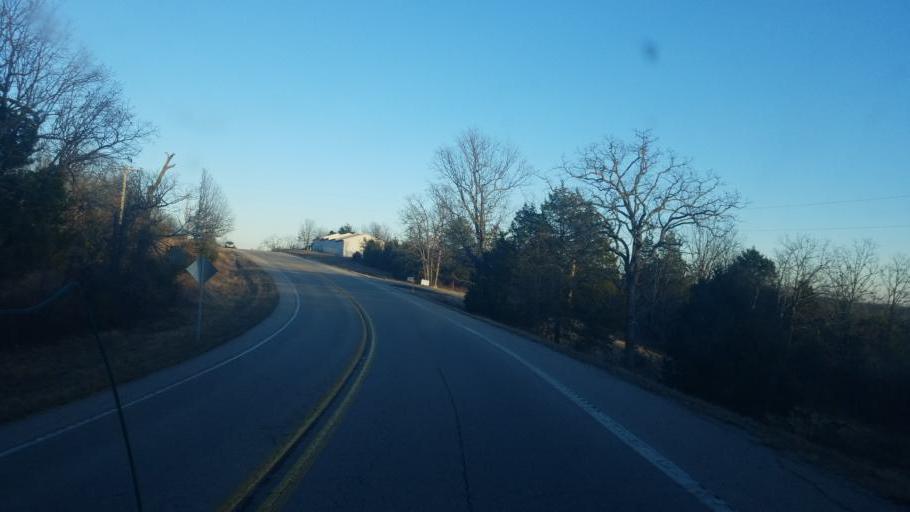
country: US
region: Arkansas
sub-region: Baxter County
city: Mountain Home
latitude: 36.3853
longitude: -92.1832
